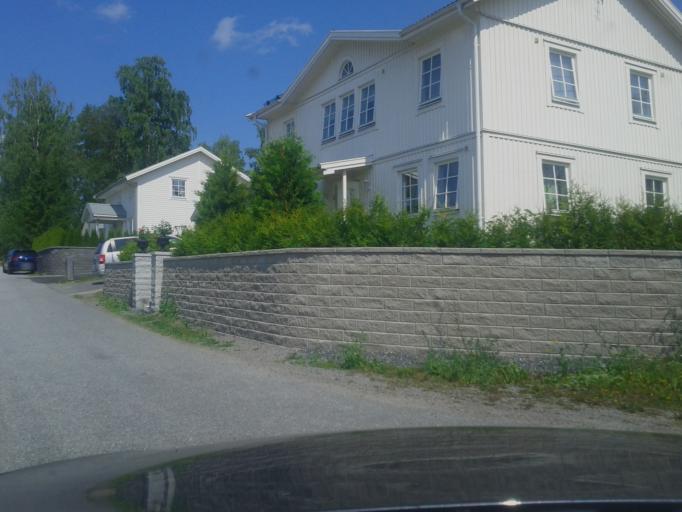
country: SE
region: Stockholm
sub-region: Vallentuna Kommun
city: Vallentuna
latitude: 59.5001
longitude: 18.0951
